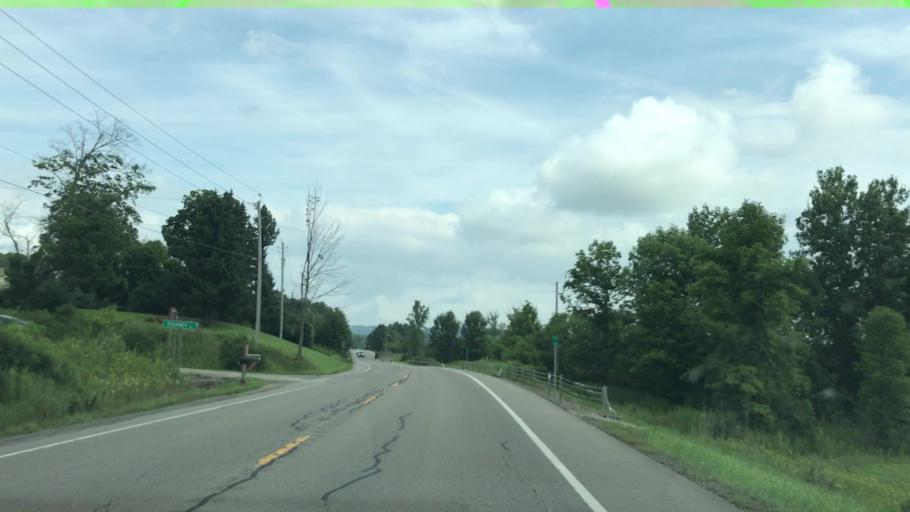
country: US
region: New York
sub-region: Steuben County
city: Bath
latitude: 42.4717
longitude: -77.2971
